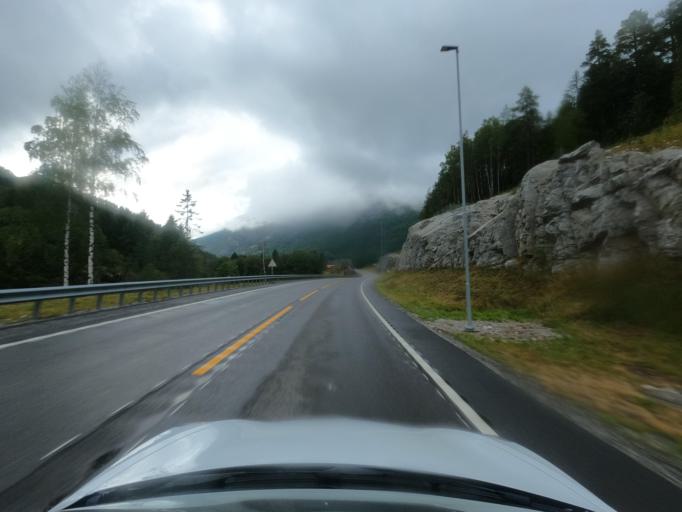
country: NO
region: Telemark
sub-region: Seljord
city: Seljord
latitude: 59.5094
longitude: 8.6466
